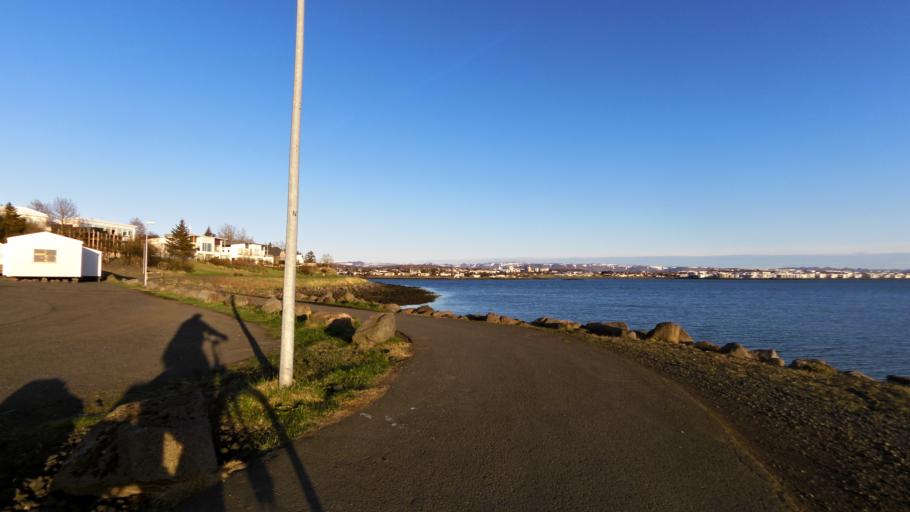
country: IS
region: Capital Region
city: Kopavogur
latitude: 64.1105
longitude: -21.9391
